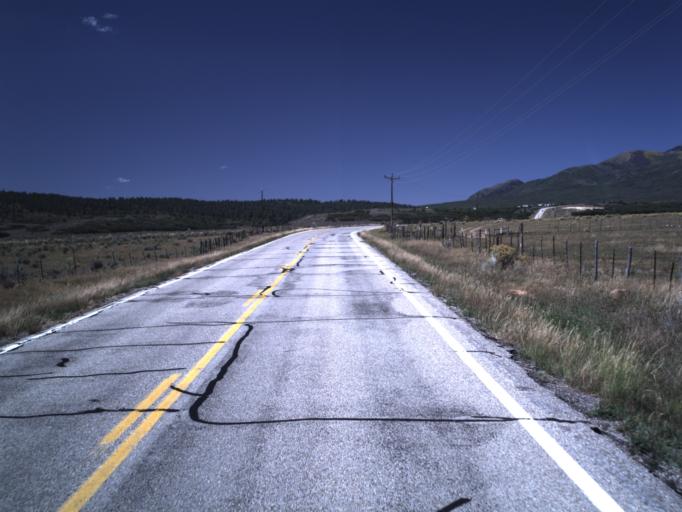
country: US
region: Utah
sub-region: Grand County
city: Moab
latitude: 38.3296
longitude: -109.1431
